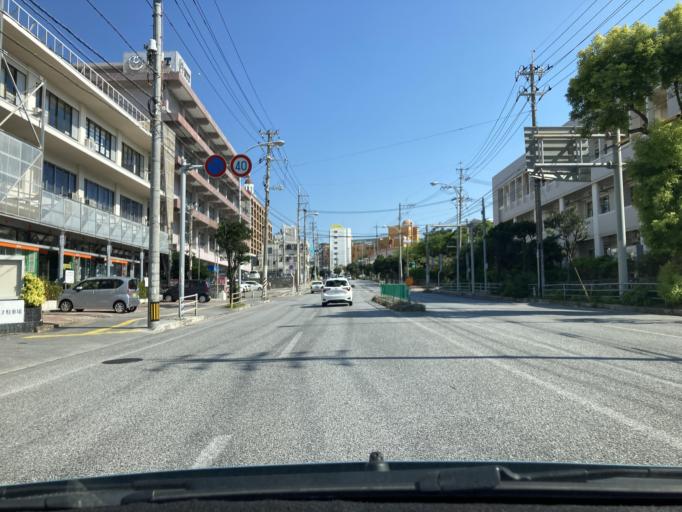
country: JP
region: Okinawa
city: Naha-shi
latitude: 26.2070
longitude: 127.6937
